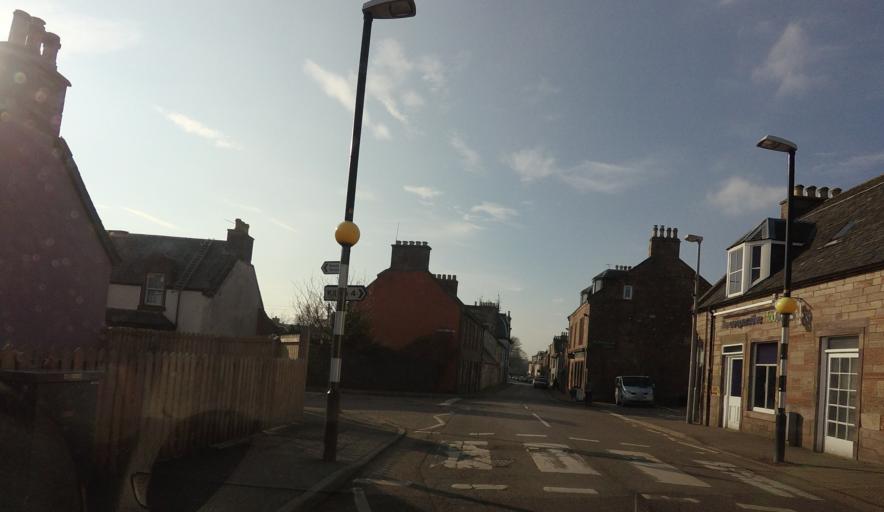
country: GB
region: Scotland
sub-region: Highland
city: Fortrose
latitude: 57.5821
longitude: -4.1296
